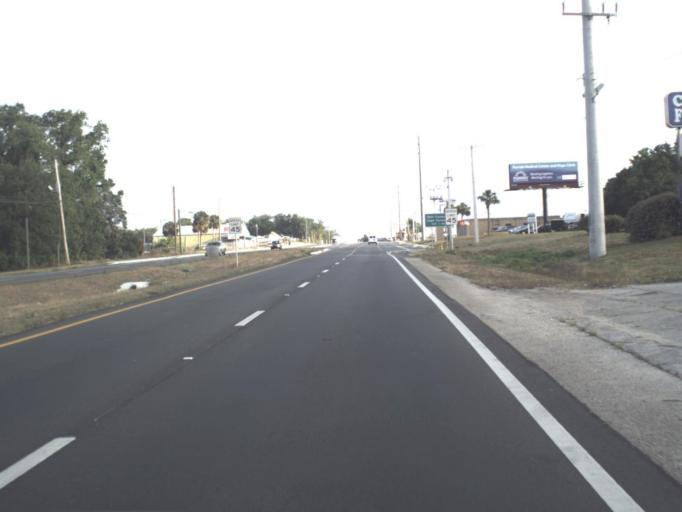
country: US
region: Florida
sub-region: Brevard County
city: Sharpes
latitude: 28.4128
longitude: -80.7552
